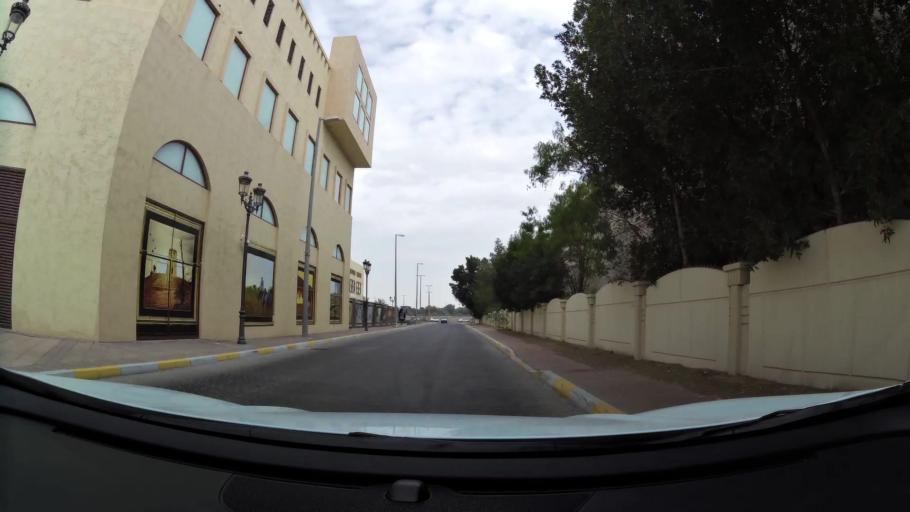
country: OM
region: Al Buraimi
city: Al Buraymi
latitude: 24.2204
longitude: 55.7827
